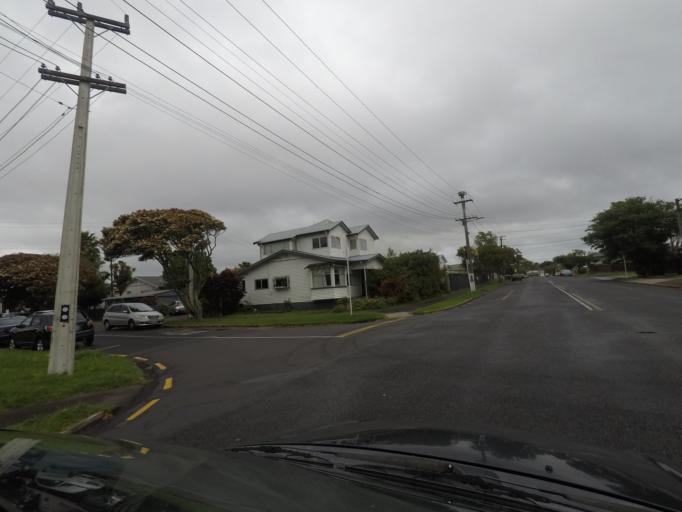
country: NZ
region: Auckland
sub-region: Auckland
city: Auckland
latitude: -36.8872
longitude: 174.7328
